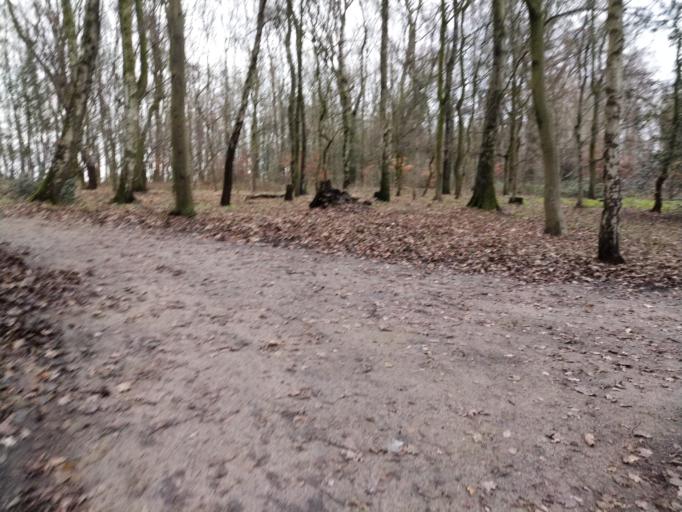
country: DE
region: North Rhine-Westphalia
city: Waltrop
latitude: 51.6059
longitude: 7.4428
